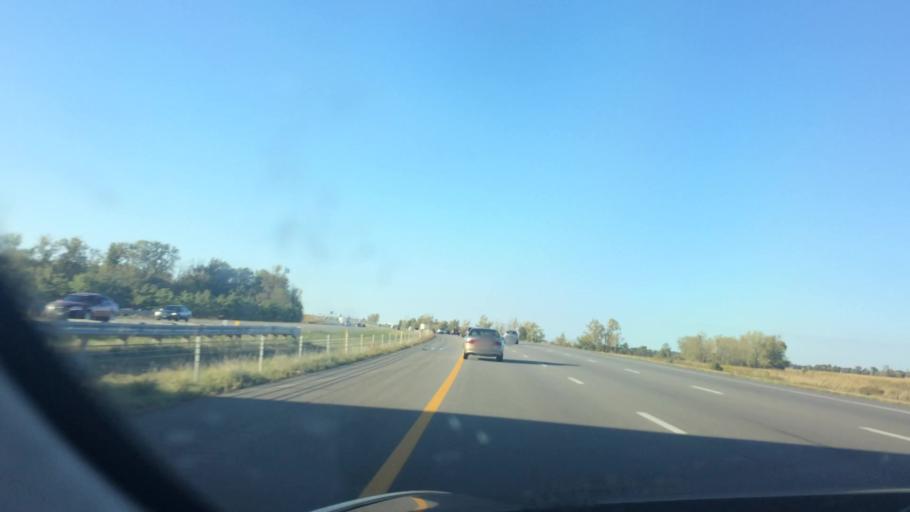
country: US
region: Ohio
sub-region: Wood County
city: Bowling Green
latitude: 41.4289
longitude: -83.6157
